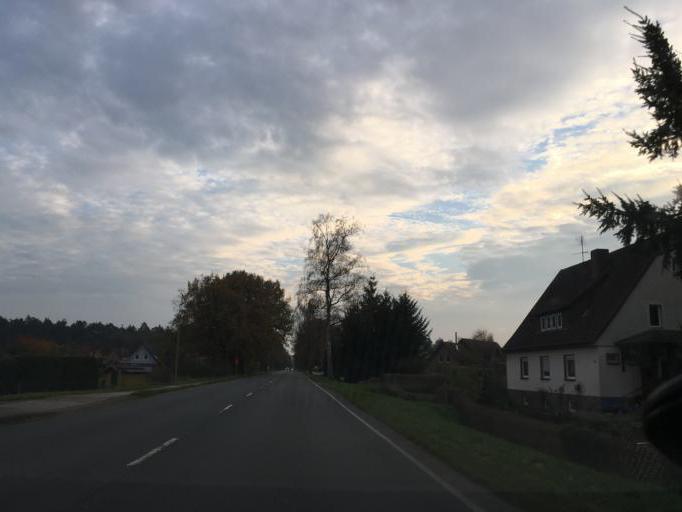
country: DE
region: Lower Saxony
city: Bergen
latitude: 52.7680
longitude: 9.9788
